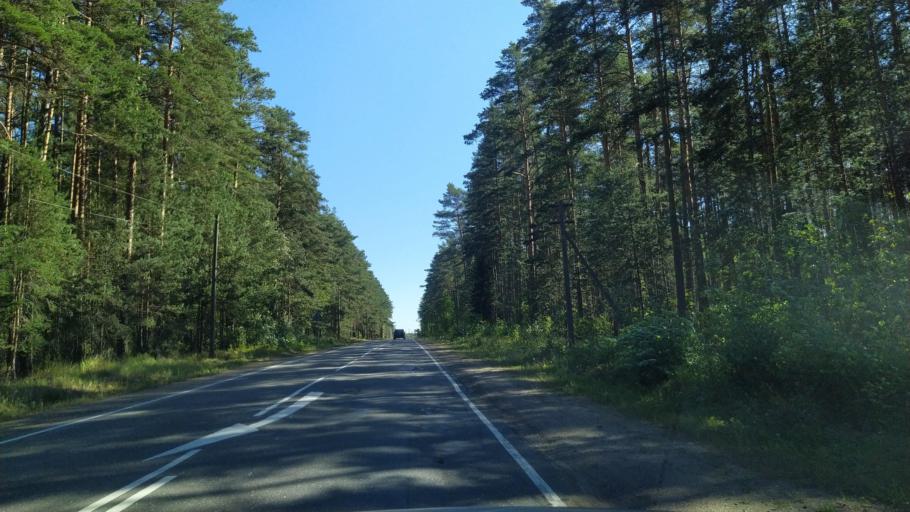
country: RU
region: Leningrad
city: Priozersk
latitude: 61.0025
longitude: 30.2078
